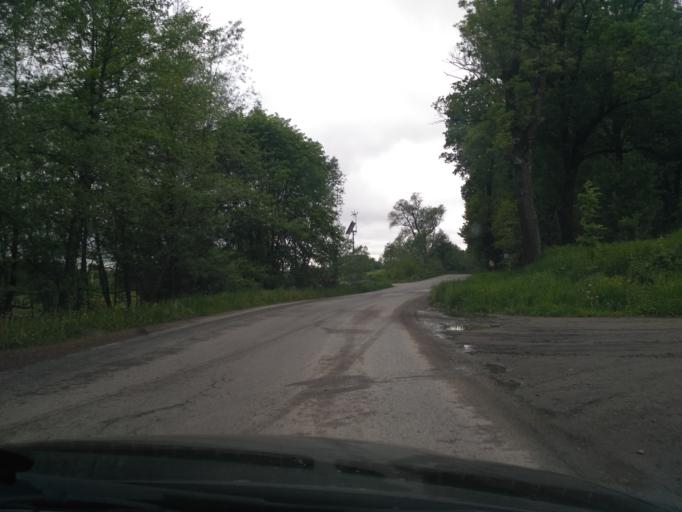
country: PL
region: Subcarpathian Voivodeship
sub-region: Powiat strzyzowski
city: Frysztak
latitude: 49.8042
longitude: 21.5553
